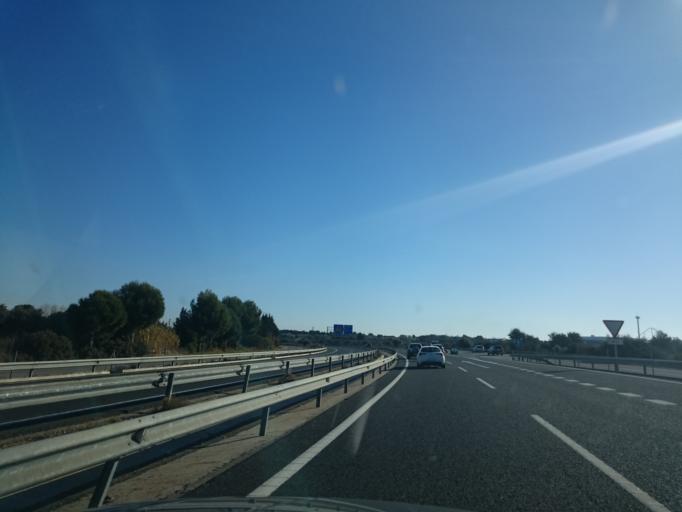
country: ES
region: Catalonia
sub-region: Provincia de Tarragona
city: Vila-seca
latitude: 41.1003
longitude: 1.1441
